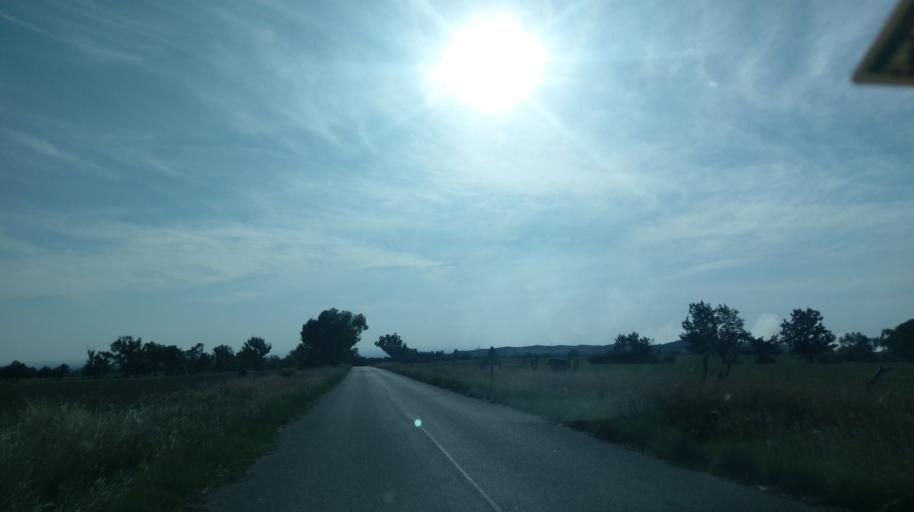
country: CY
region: Ammochostos
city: Lefkonoiko
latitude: 35.3037
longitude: 33.7472
